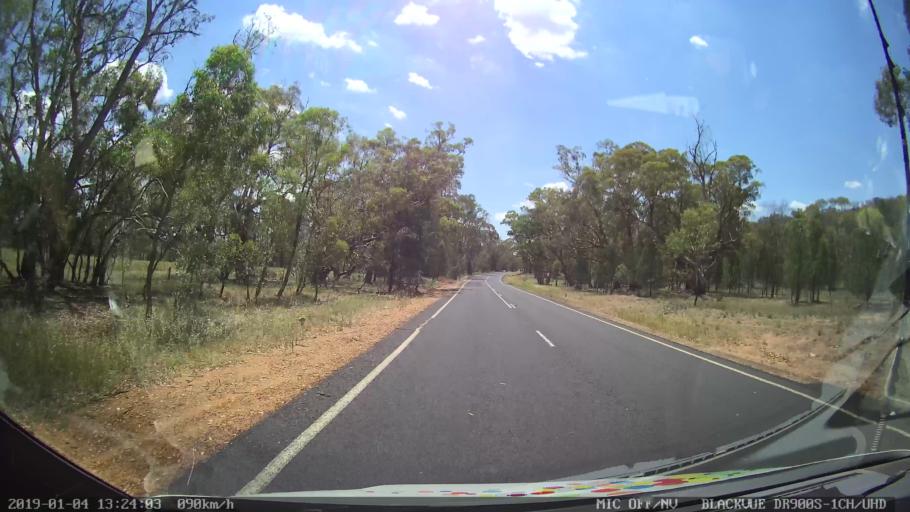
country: AU
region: New South Wales
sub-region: Parkes
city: Peak Hill
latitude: -32.7104
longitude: 148.5518
